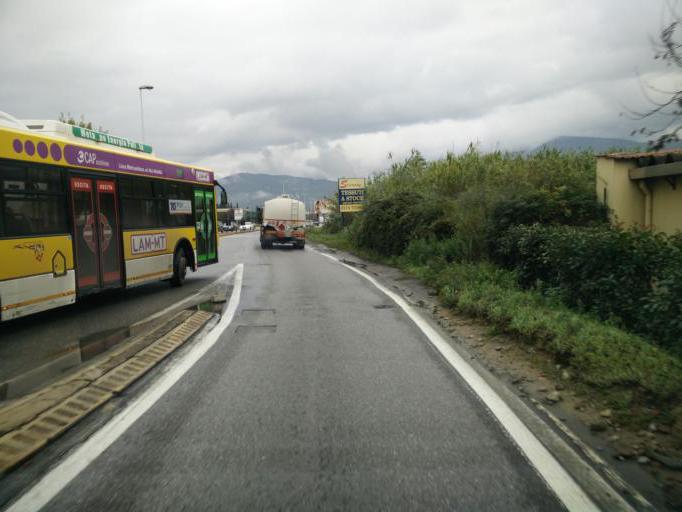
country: IT
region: Tuscany
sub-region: Provincia di Prato
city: Prato
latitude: 43.8937
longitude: 11.0751
